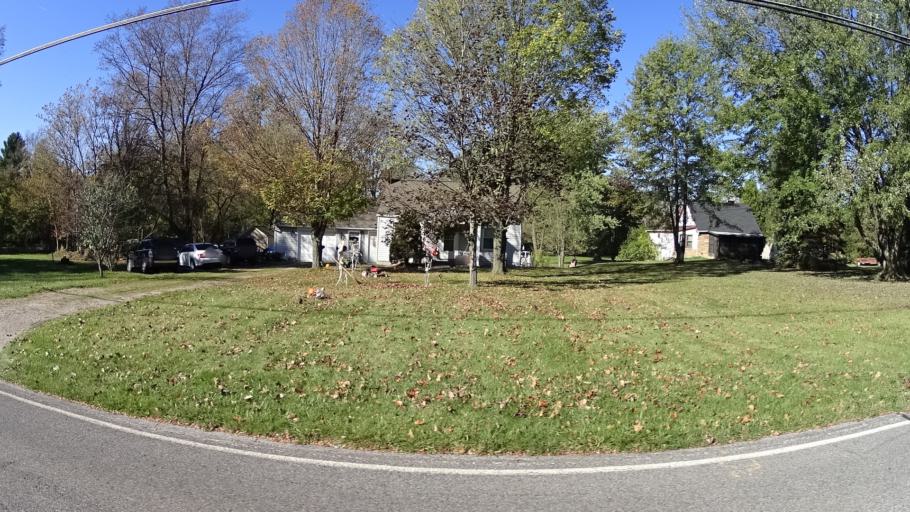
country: US
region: Ohio
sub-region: Lorain County
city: South Amherst
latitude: 41.3504
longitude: -82.2301
